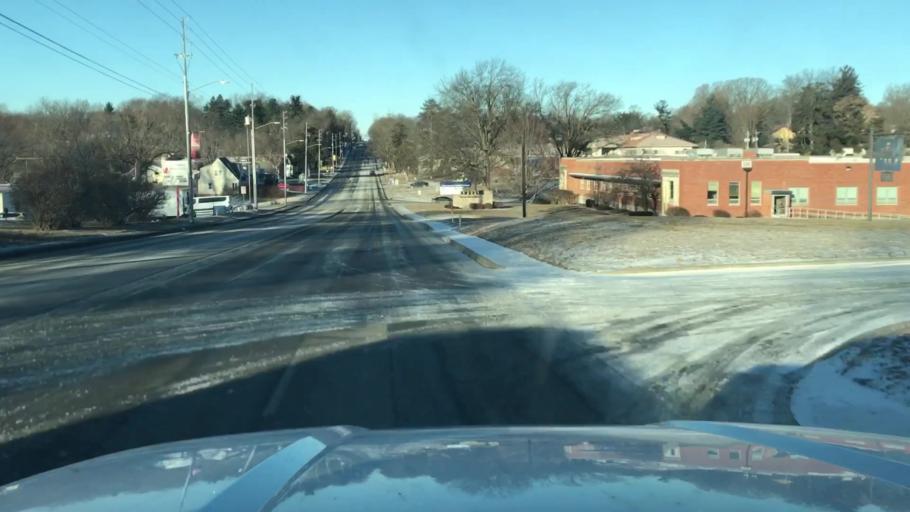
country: US
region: Missouri
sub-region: Buchanan County
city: Saint Joseph
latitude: 39.7770
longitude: -94.8149
